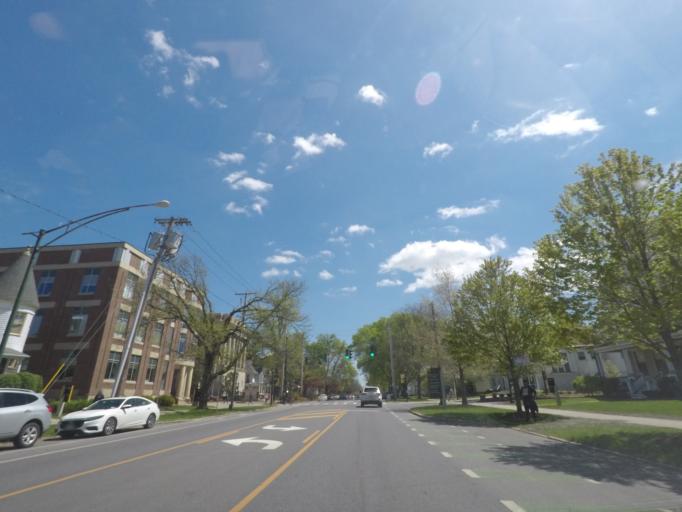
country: US
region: New York
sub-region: Albany County
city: West Albany
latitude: 42.6639
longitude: -73.7878
